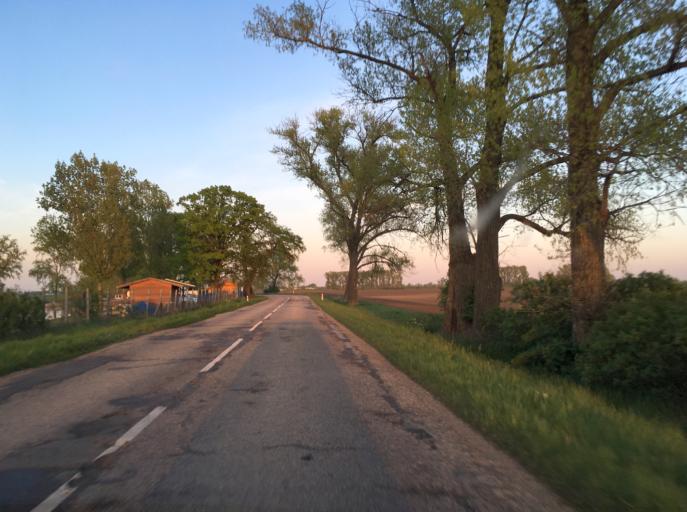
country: SK
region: Nitriansky
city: Kolarovo
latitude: 47.9022
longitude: 17.9345
